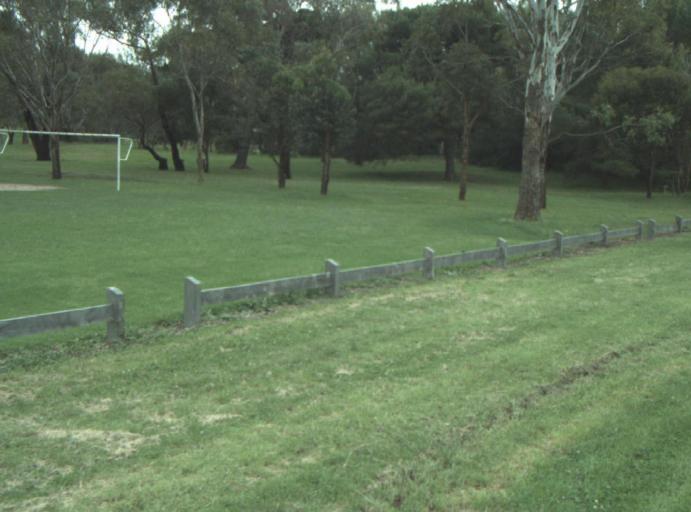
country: AU
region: Victoria
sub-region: Greater Geelong
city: East Geelong
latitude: -38.1536
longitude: 144.3845
